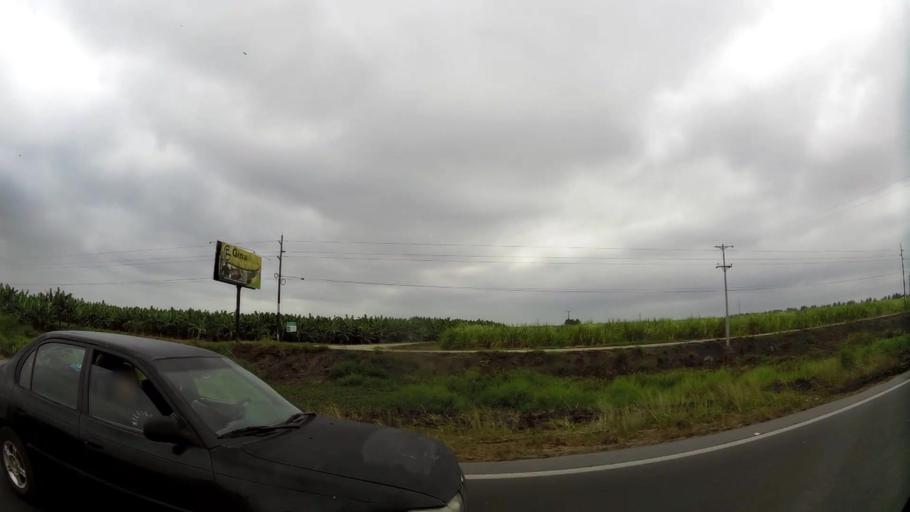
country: EC
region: Guayas
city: Yaguachi Nuevo
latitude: -2.2901
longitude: -79.6395
